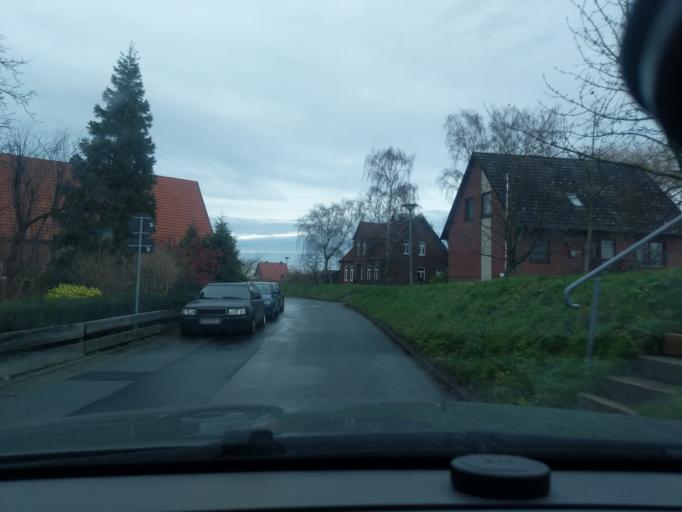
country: DE
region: Lower Saxony
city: Mittelnkirchen
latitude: 53.5319
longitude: 9.6122
